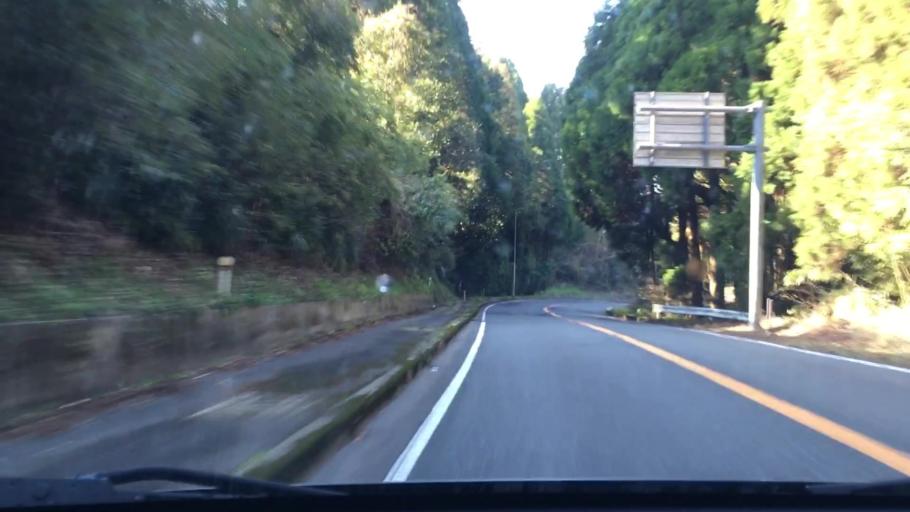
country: JP
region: Kagoshima
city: Sueyoshicho-ninokata
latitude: 31.6734
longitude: 130.9246
